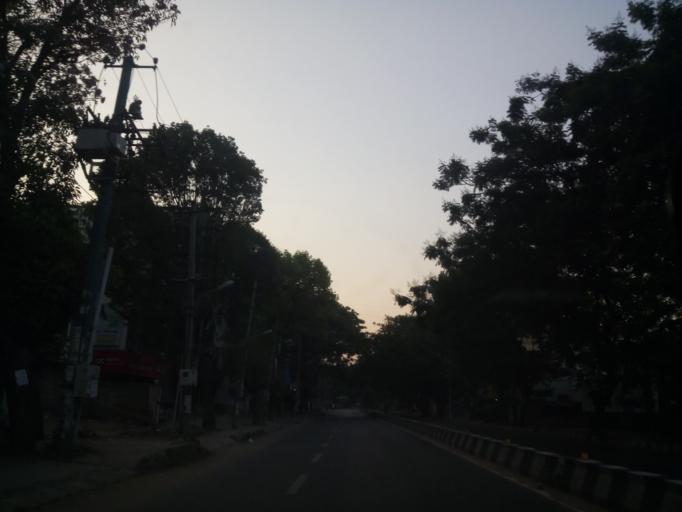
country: IN
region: Karnataka
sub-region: Bangalore Urban
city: Bangalore
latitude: 12.9335
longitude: 77.6306
